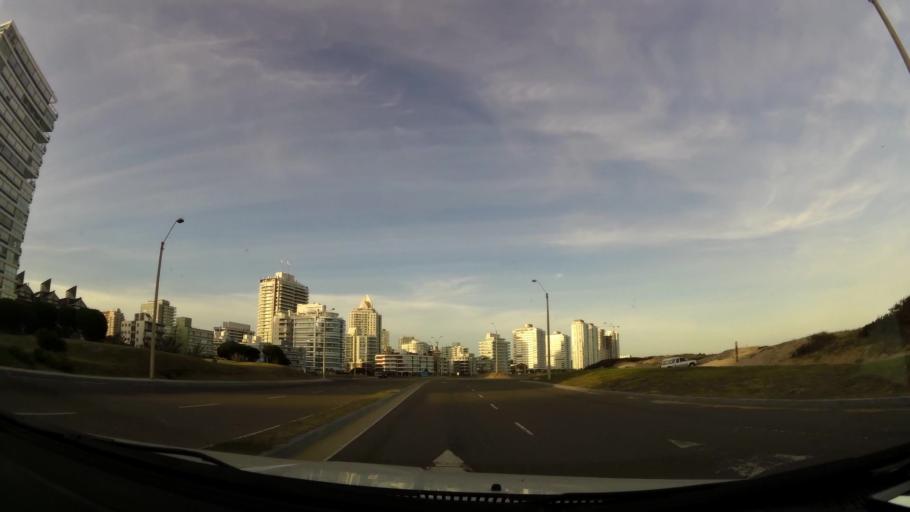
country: UY
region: Maldonado
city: Punta del Este
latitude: -34.9527
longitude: -54.9291
